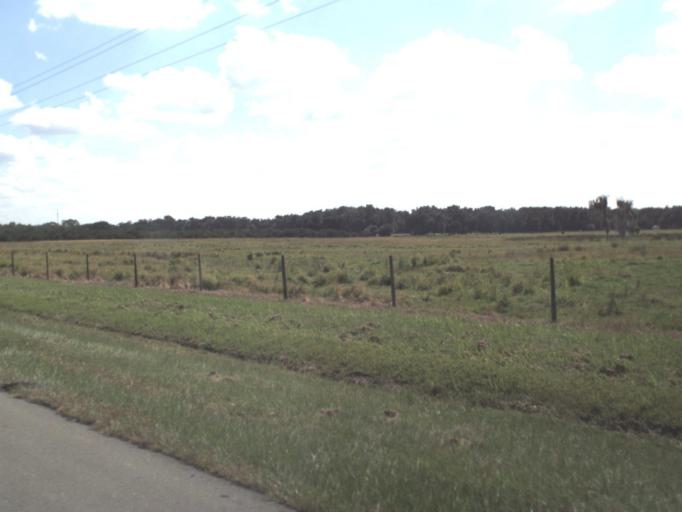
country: US
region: Florida
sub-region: Hardee County
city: Zolfo Springs
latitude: 27.4607
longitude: -81.6928
